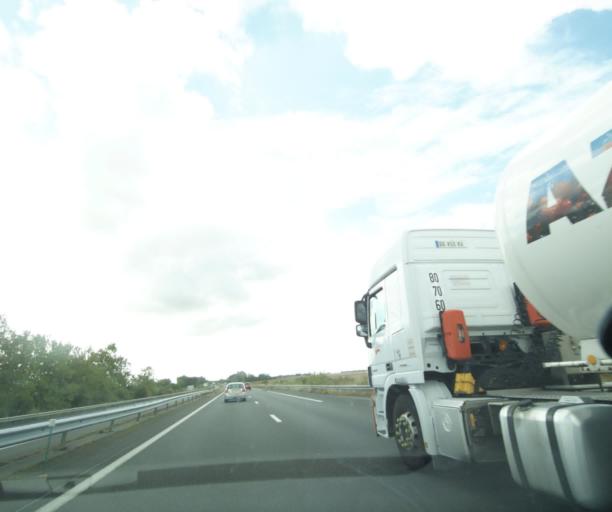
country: FR
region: Poitou-Charentes
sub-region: Departement de la Charente-Maritime
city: Thenac
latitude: 45.6847
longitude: -0.6453
